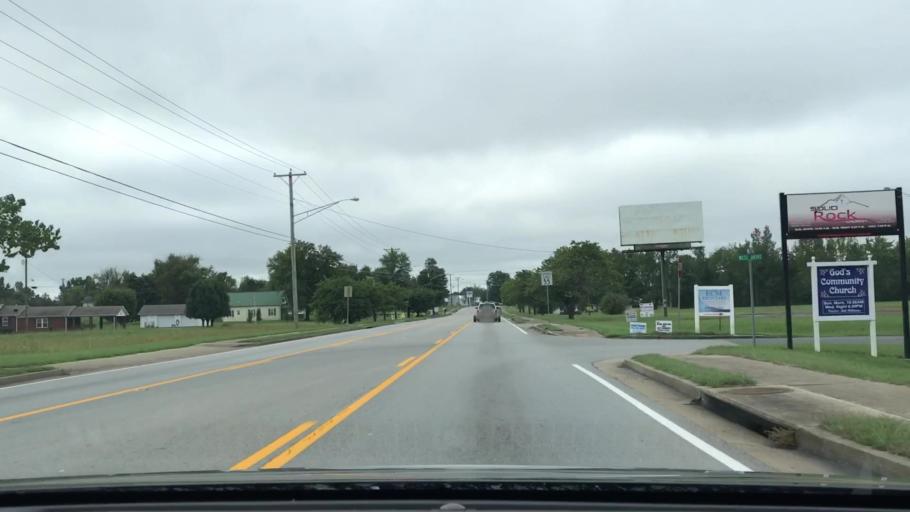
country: US
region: Kentucky
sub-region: Russell County
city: Russell Springs
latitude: 37.0247
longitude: -85.0769
